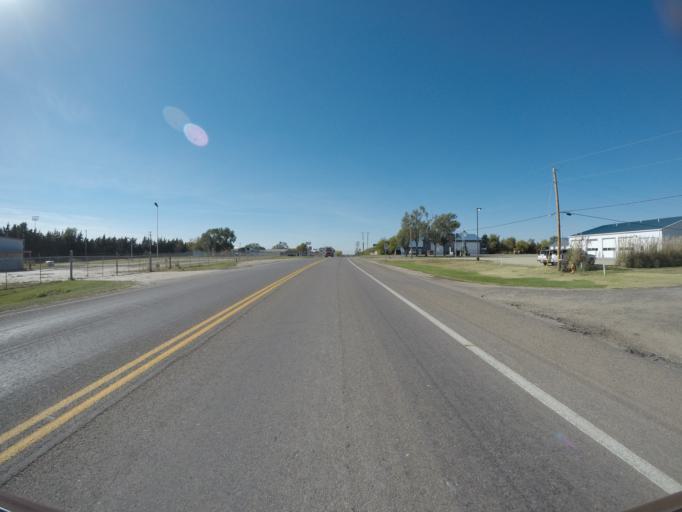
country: US
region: Kansas
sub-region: Smith County
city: Smith Center
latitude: 39.7852
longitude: -98.7734
